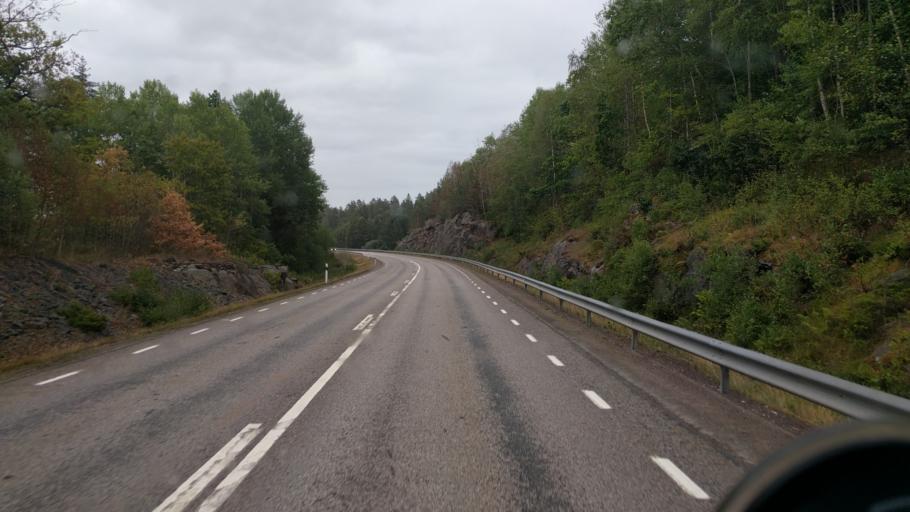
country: SE
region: Kalmar
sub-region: Vasterviks Kommun
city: Ankarsrum
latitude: 57.6965
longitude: 16.2837
